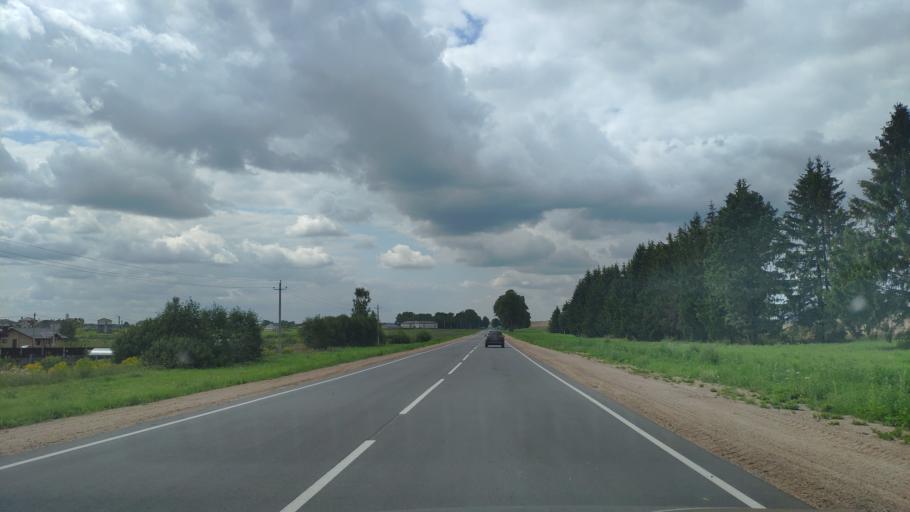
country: BY
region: Minsk
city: Zaslawye
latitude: 54.0053
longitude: 27.3475
